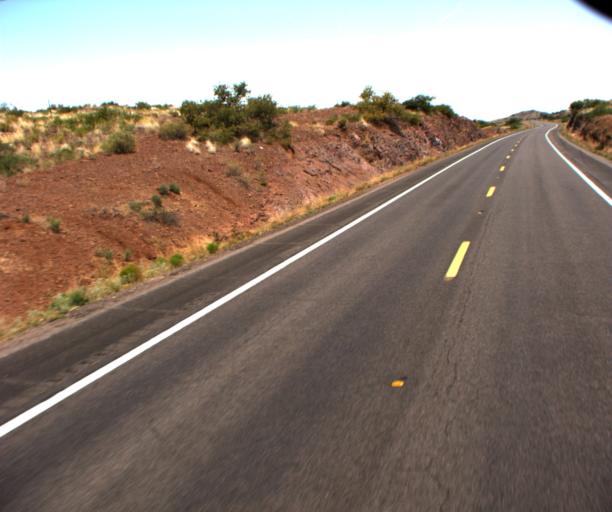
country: US
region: Arizona
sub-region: Greenlee County
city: Clifton
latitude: 32.7658
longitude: -109.2532
